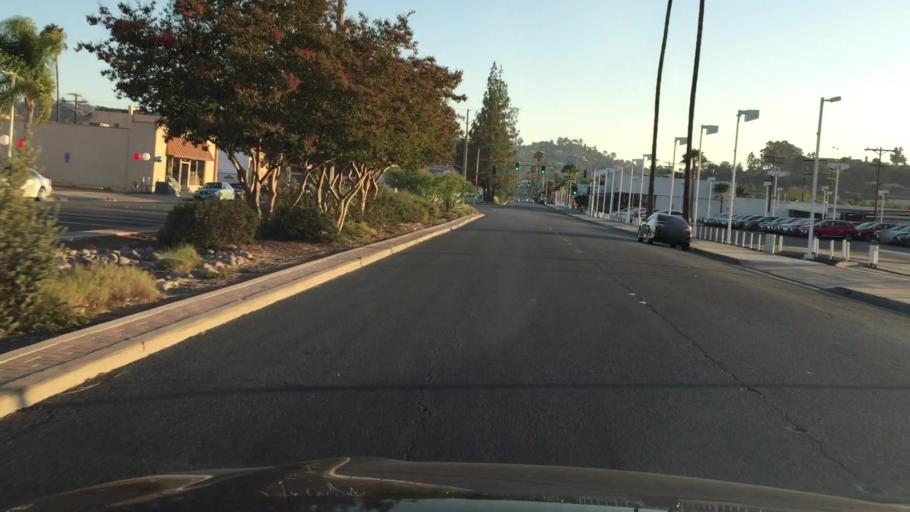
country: US
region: California
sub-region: San Diego County
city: El Cajon
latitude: 32.7939
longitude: -116.9689
